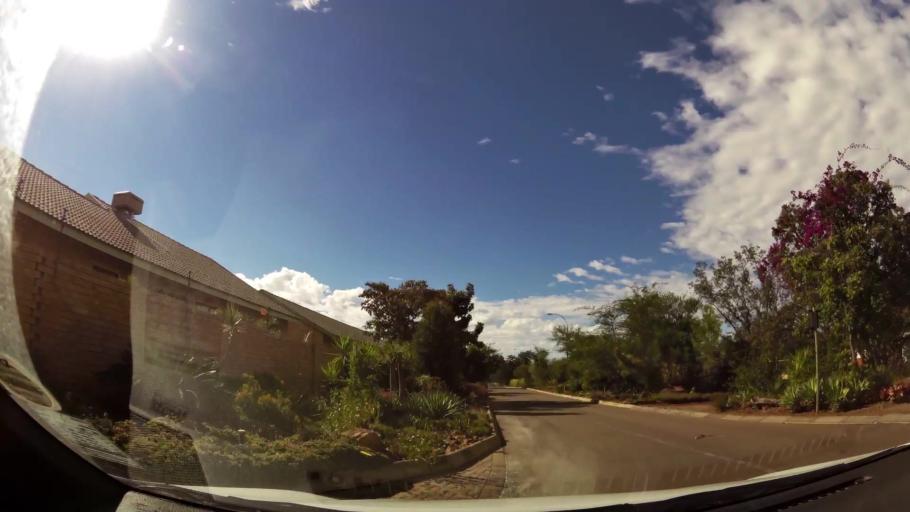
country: ZA
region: Limpopo
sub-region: Waterberg District Municipality
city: Warmbaths
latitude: -24.8707
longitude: 28.2851
